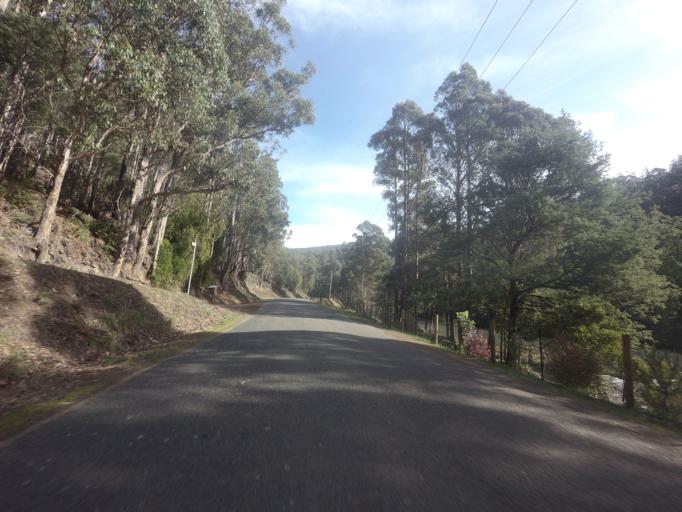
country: AU
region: Tasmania
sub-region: Huon Valley
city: Huonville
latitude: -43.0405
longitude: 147.1331
